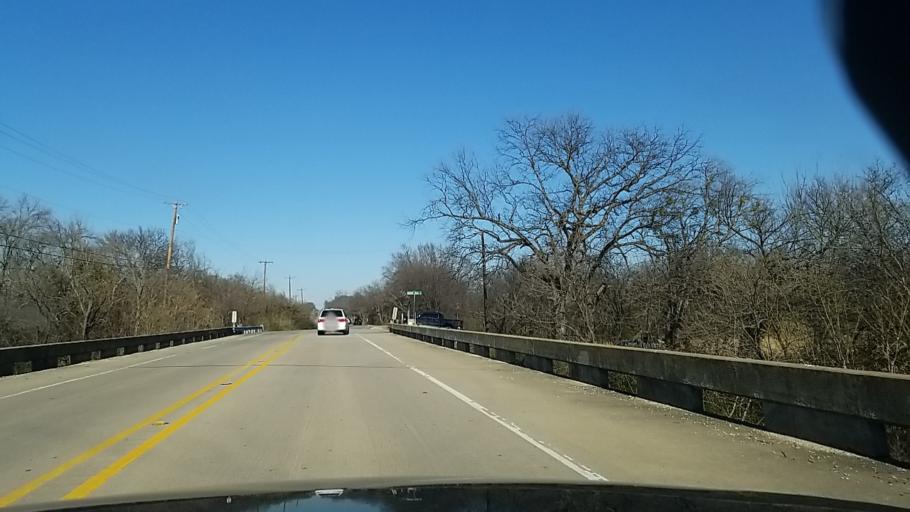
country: US
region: Texas
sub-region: Denton County
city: Argyle
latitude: 33.1513
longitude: -97.1419
